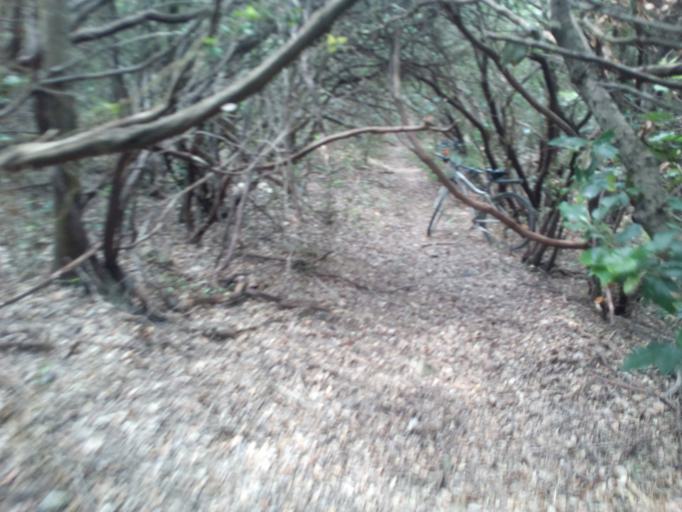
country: FR
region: Provence-Alpes-Cote d'Azur
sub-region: Departement du Var
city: La Londe-les-Maures
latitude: 43.0159
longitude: 6.2387
